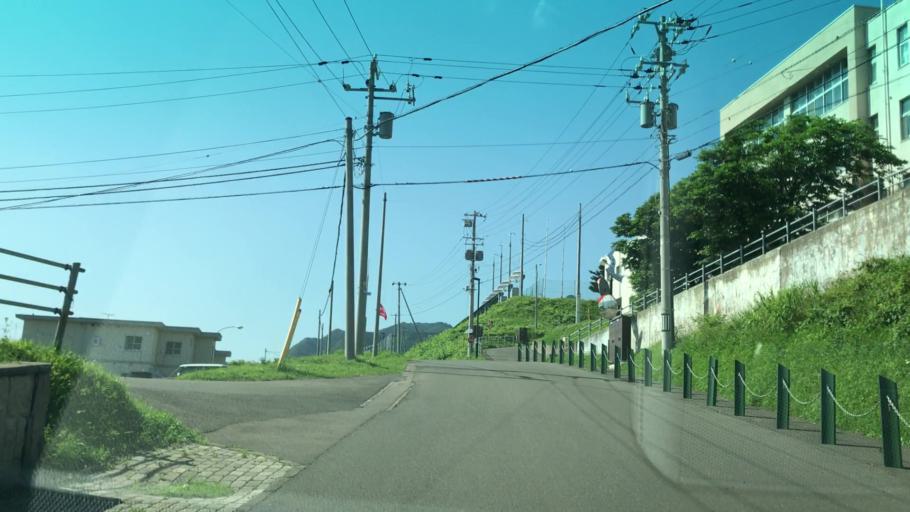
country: JP
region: Hokkaido
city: Iwanai
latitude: 43.1442
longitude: 140.4252
